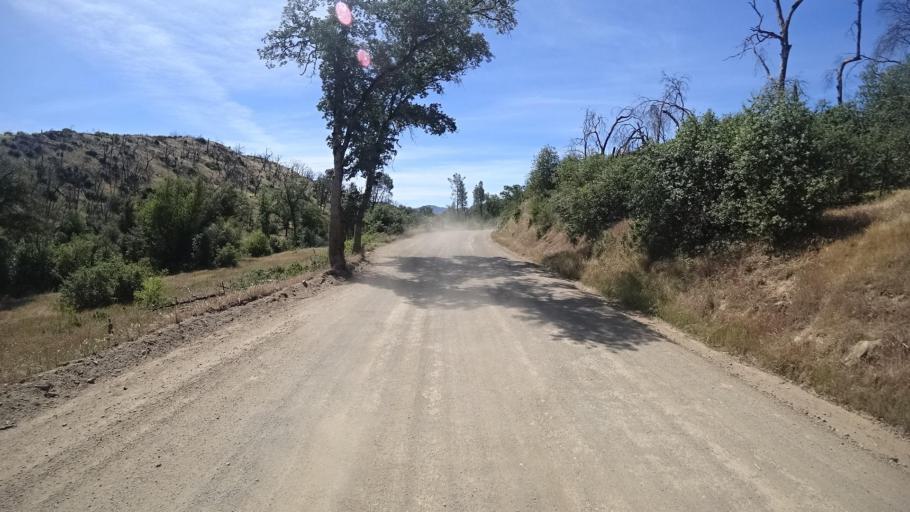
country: US
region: California
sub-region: Lake County
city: Middletown
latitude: 38.8036
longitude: -122.6147
